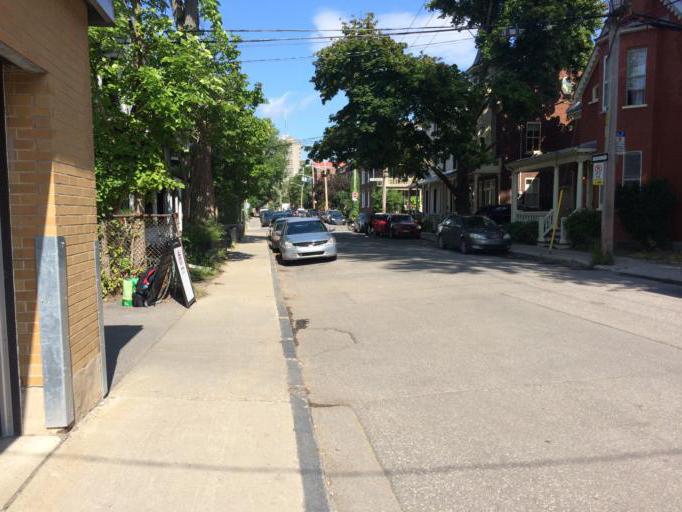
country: CA
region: Quebec
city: Quebec
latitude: 46.8023
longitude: -71.2283
